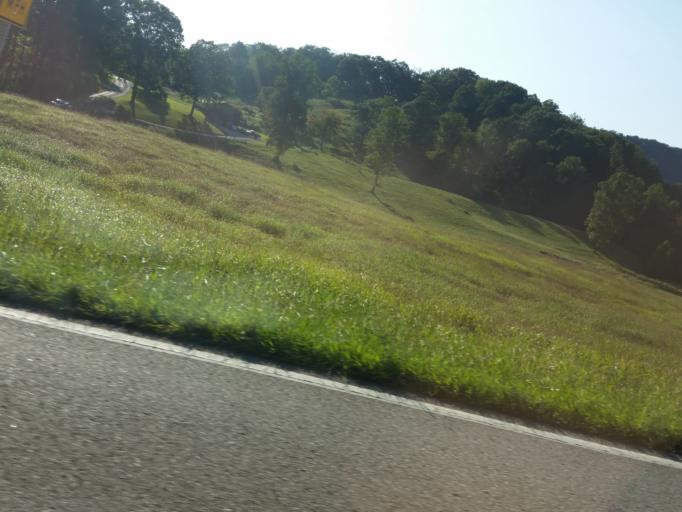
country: US
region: Tennessee
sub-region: Union County
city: Luttrell
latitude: 36.2335
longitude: -83.7437
